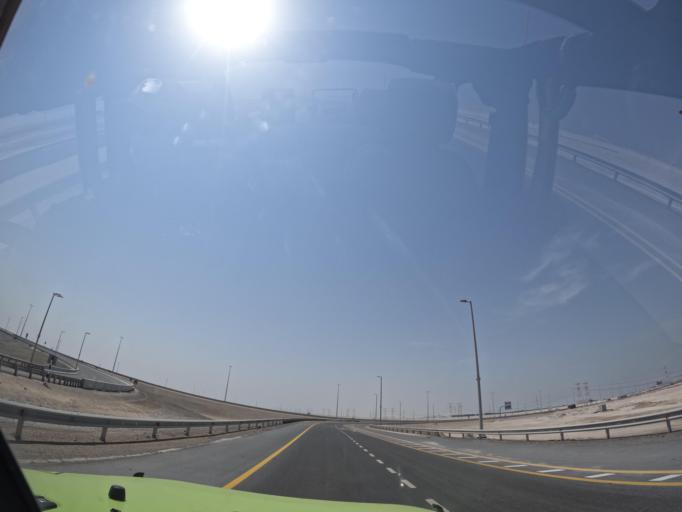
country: AE
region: Abu Dhabi
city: Abu Dhabi
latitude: 24.2499
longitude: 54.4722
